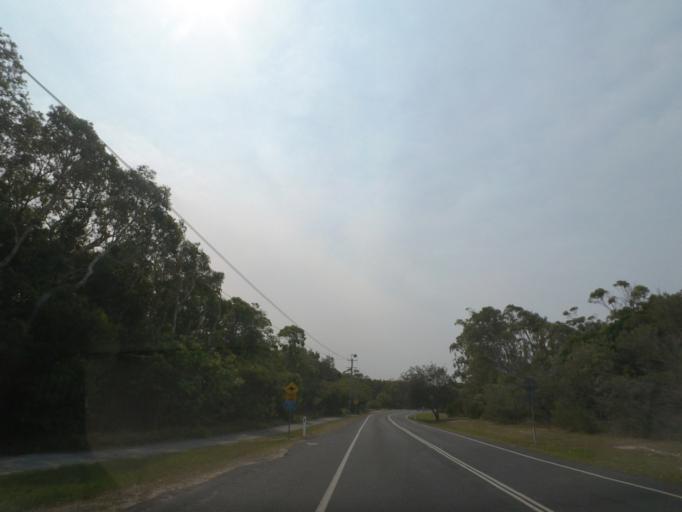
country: AU
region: New South Wales
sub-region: Tweed
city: Pottsville Beach
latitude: -28.3543
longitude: 153.5720
